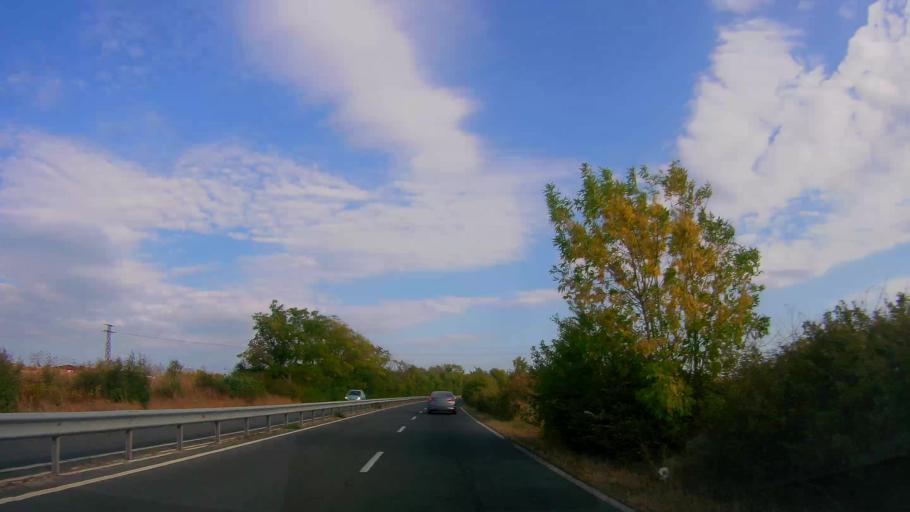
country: BG
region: Burgas
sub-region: Obshtina Sozopol
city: Chernomorets
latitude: 42.4336
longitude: 27.6379
